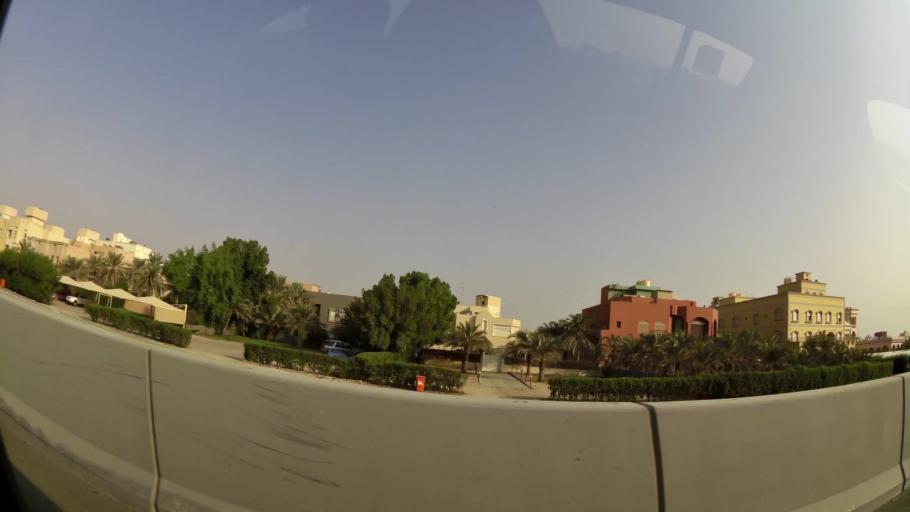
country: KW
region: Al Asimah
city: Ar Rabiyah
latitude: 29.3097
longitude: 47.8793
